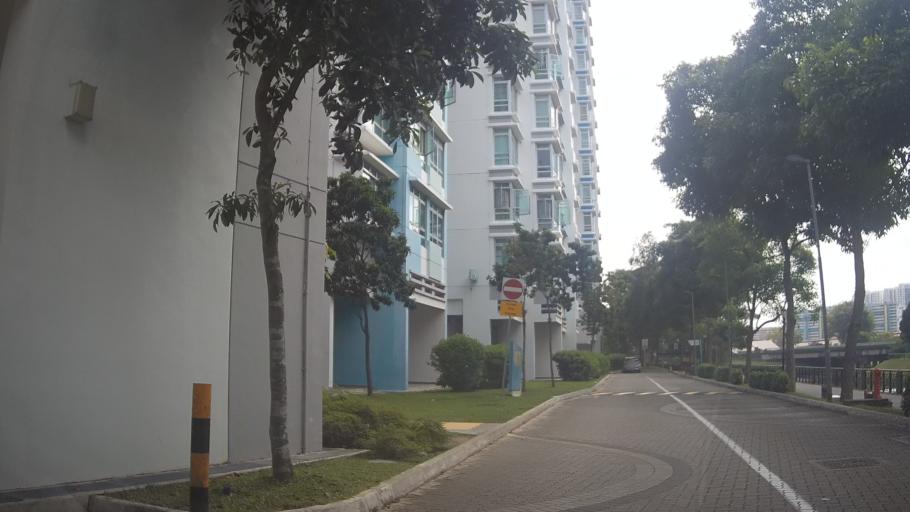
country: SG
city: Singapore
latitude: 1.3203
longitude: 103.8658
